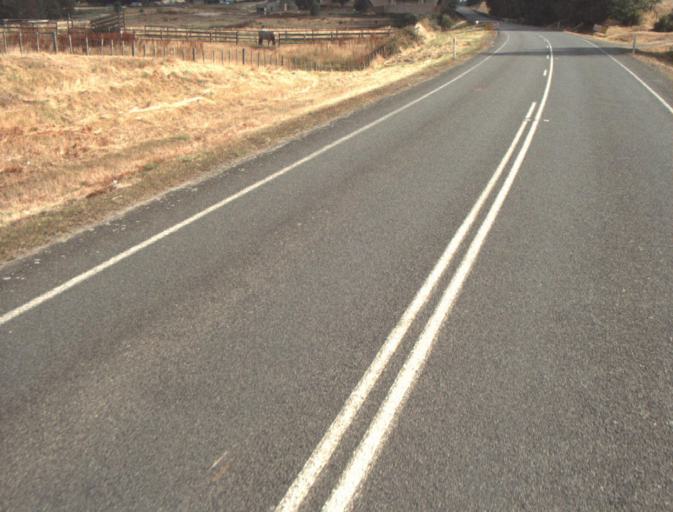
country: AU
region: Tasmania
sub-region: Launceston
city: Mayfield
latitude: -41.2909
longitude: 147.2168
